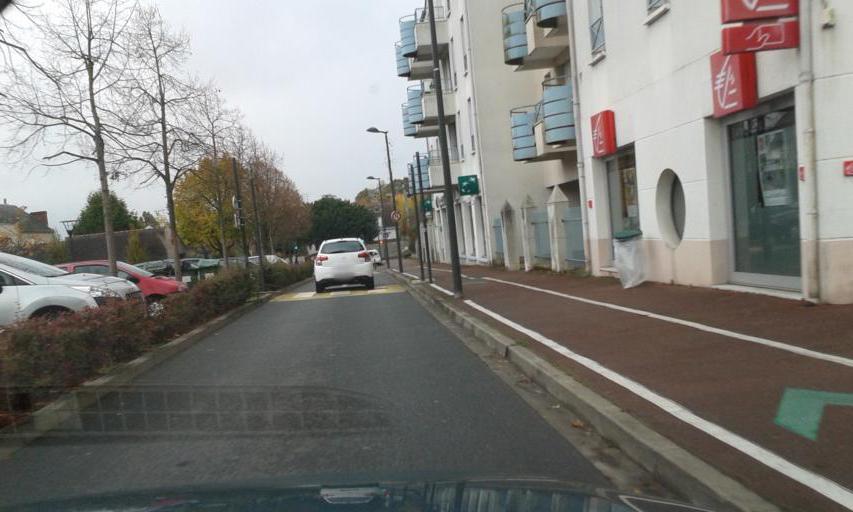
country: FR
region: Centre
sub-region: Departement du Loiret
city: Olivet
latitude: 47.8657
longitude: 1.9027
